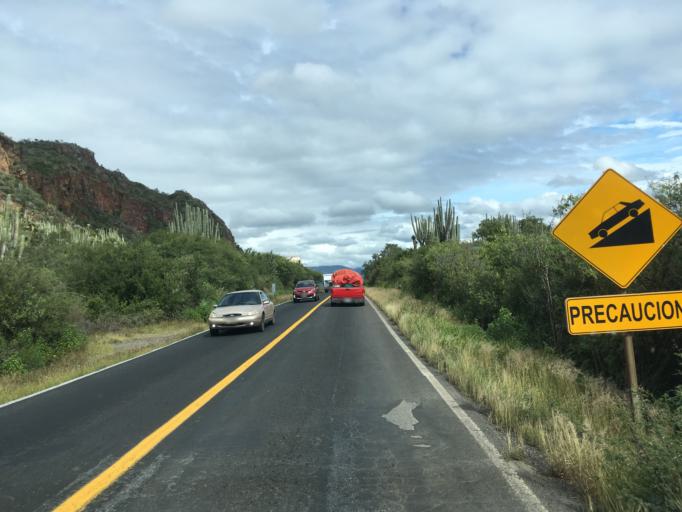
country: MX
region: Hidalgo
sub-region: San Agustin Metzquititlan
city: Mezquititlan
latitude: 20.4289
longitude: -98.6861
